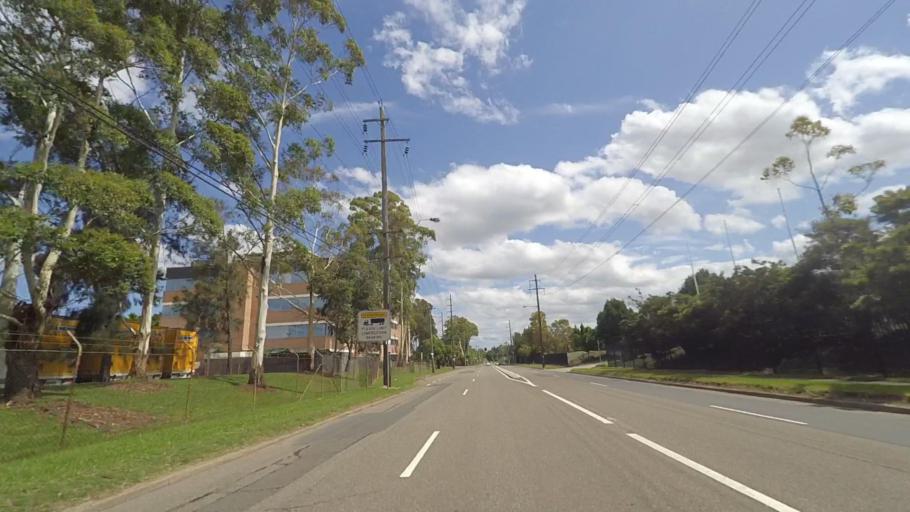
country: AU
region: New South Wales
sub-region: Holroyd
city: Guildford West
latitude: -33.8564
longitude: 150.9590
